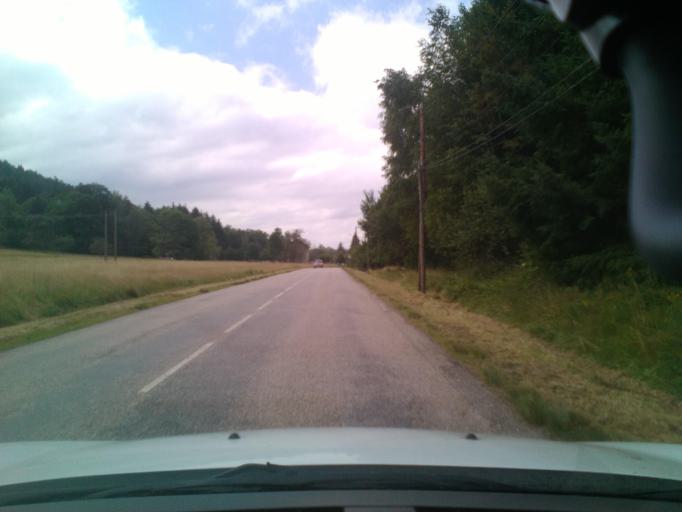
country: FR
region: Lorraine
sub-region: Departement des Vosges
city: Granges-sur-Vologne
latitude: 48.1312
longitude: 6.8218
